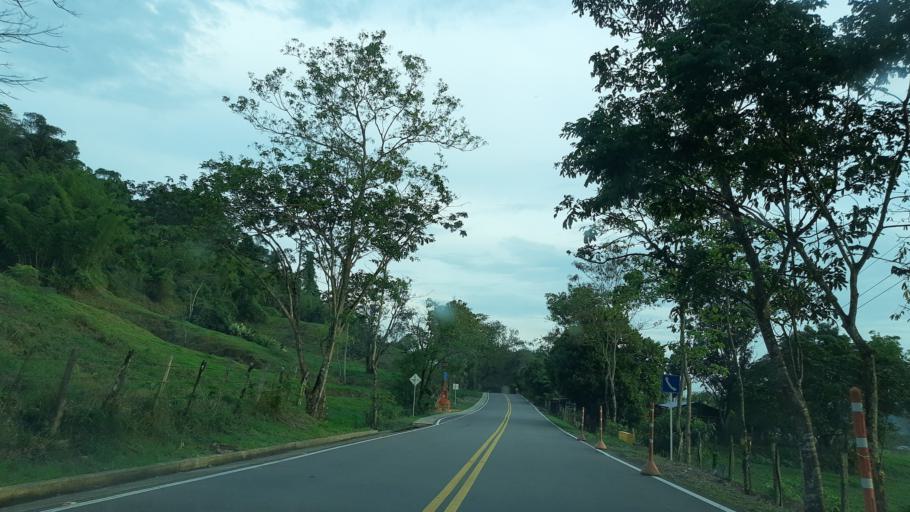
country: CO
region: Casanare
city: Sabanalarga
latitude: 4.7889
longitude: -73.0527
